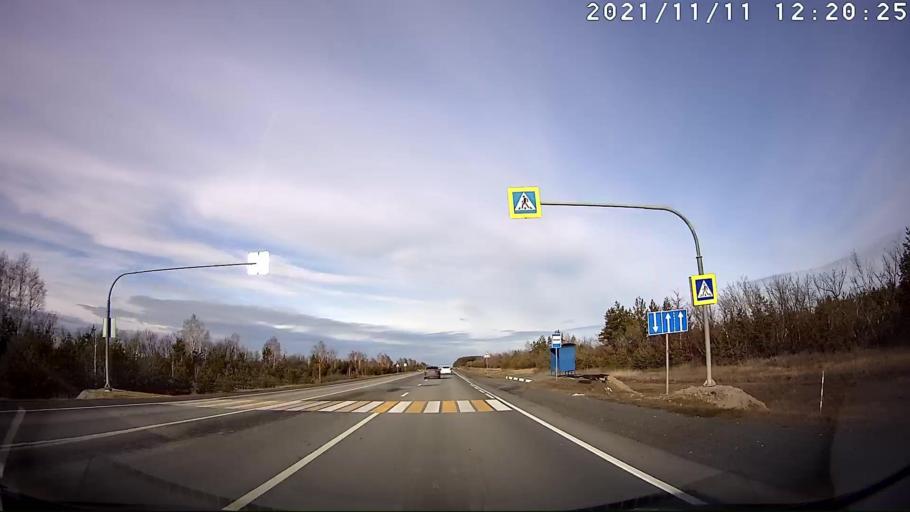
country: RU
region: Ulyanovsk
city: Silikatnyy
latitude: 53.8812
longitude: 48.2760
